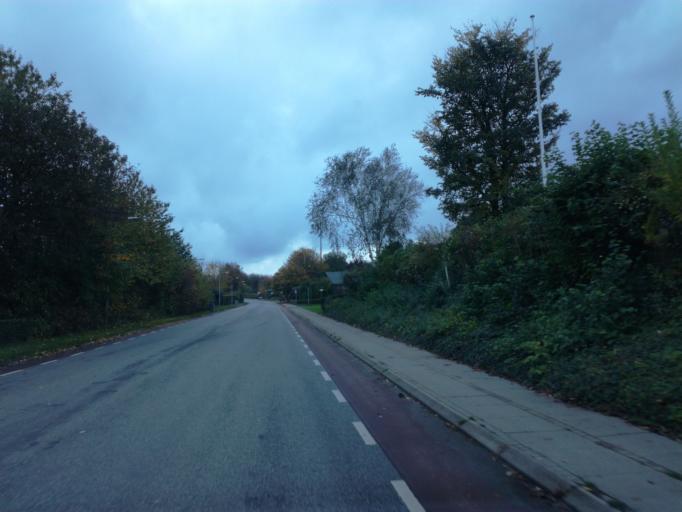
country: DK
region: South Denmark
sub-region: Vejle Kommune
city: Borkop
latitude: 55.6391
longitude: 9.6529
